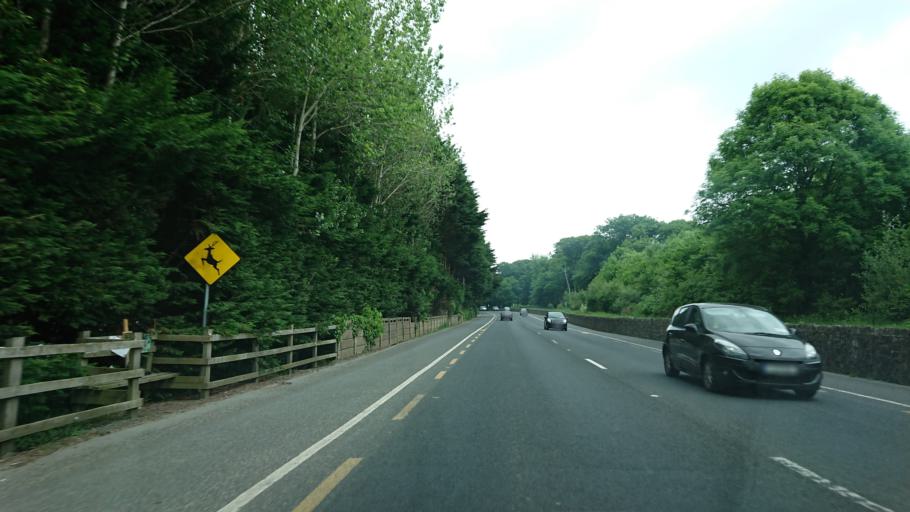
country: IE
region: Munster
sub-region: Waterford
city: Waterford
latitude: 52.2072
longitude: -7.1162
